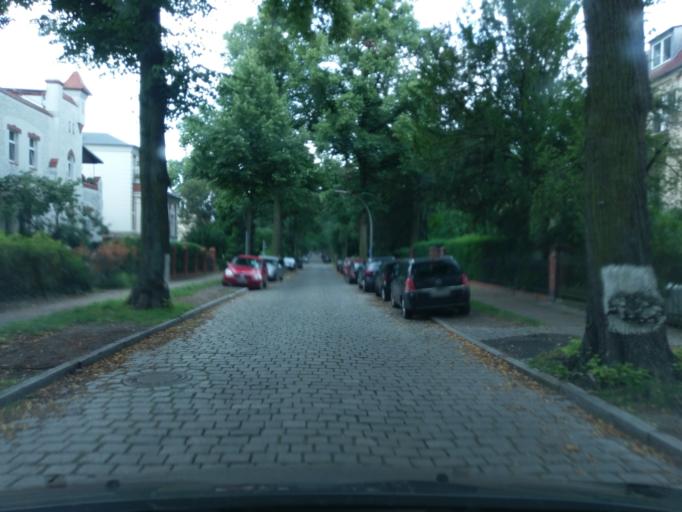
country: DE
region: Berlin
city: Lichterfelde
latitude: 52.4429
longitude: 13.3047
